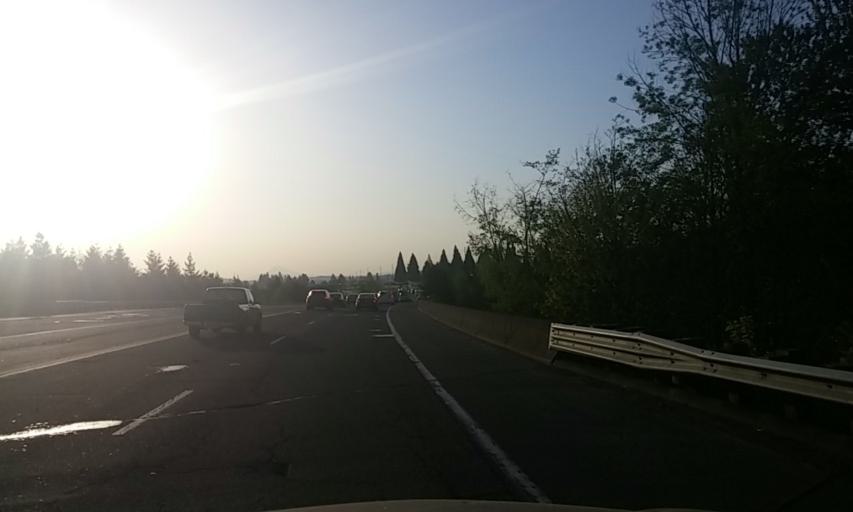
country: US
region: Oregon
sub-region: Washington County
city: Aloha
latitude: 45.4915
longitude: -122.8376
